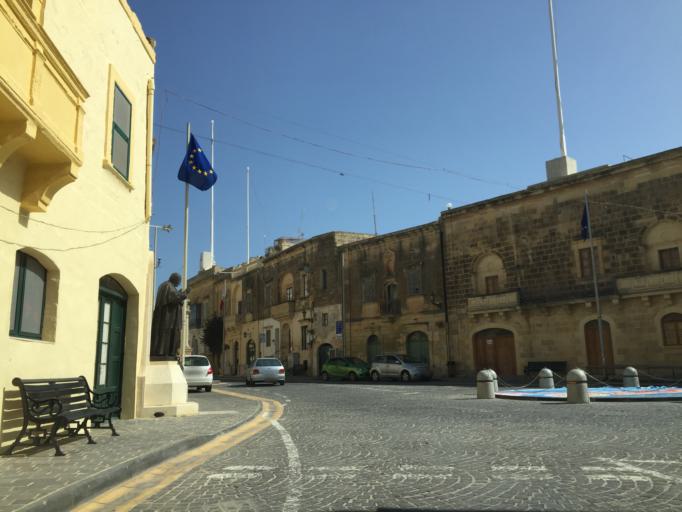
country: MT
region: L-Gharb
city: Gharb
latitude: 36.0600
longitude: 14.2091
